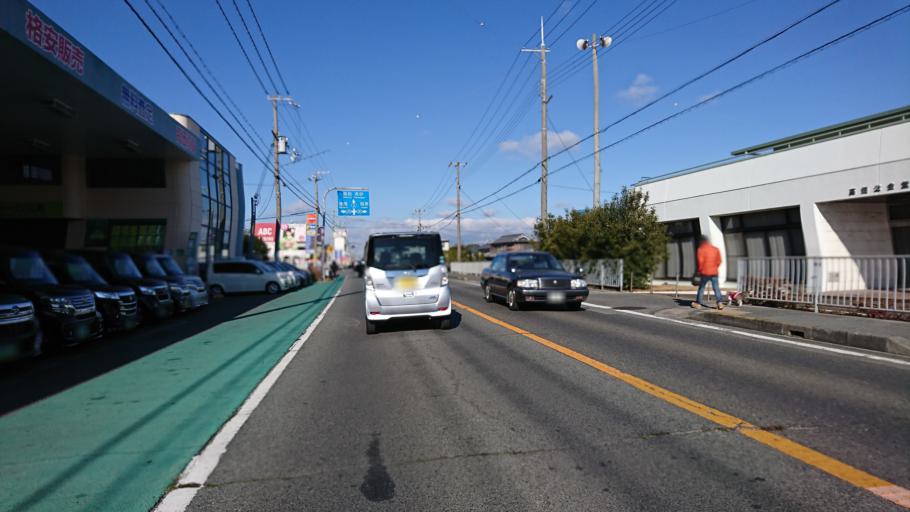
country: JP
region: Hyogo
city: Kakogawacho-honmachi
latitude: 34.7333
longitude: 134.8770
